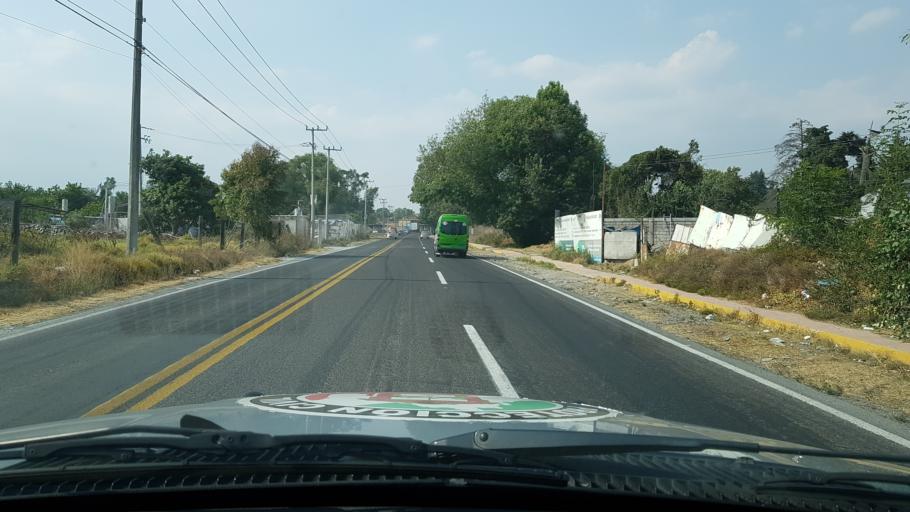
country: MX
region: Mexico
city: Tepetlixpa
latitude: 19.0184
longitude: -98.8245
